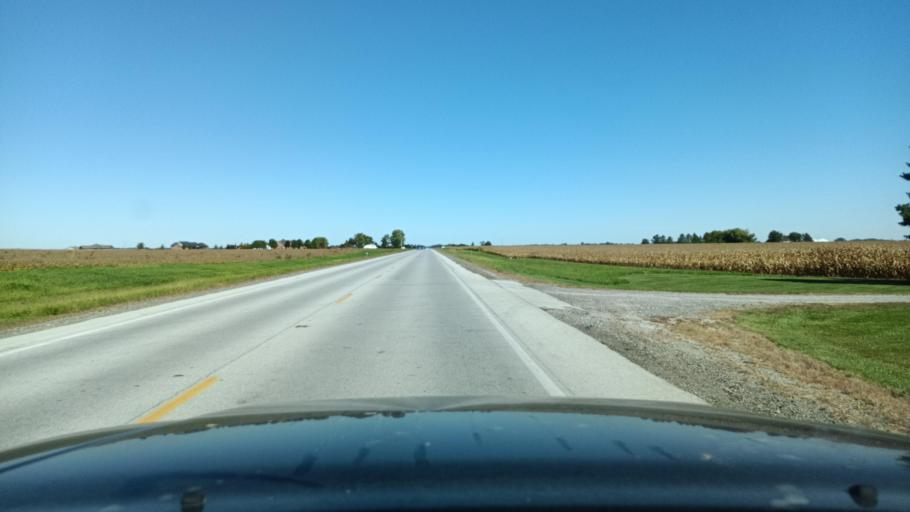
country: US
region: Illinois
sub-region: Champaign County
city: Philo
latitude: 40.0348
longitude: -88.1616
